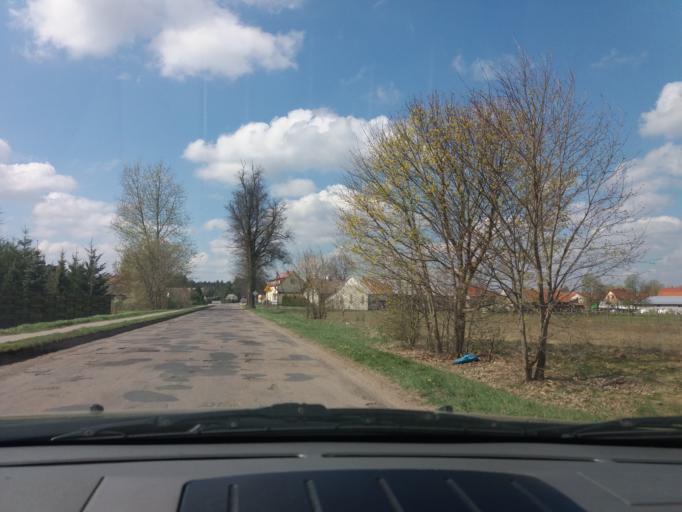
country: PL
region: Warmian-Masurian Voivodeship
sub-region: Powiat szczycienski
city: Jedwabno
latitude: 53.3629
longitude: 20.6383
